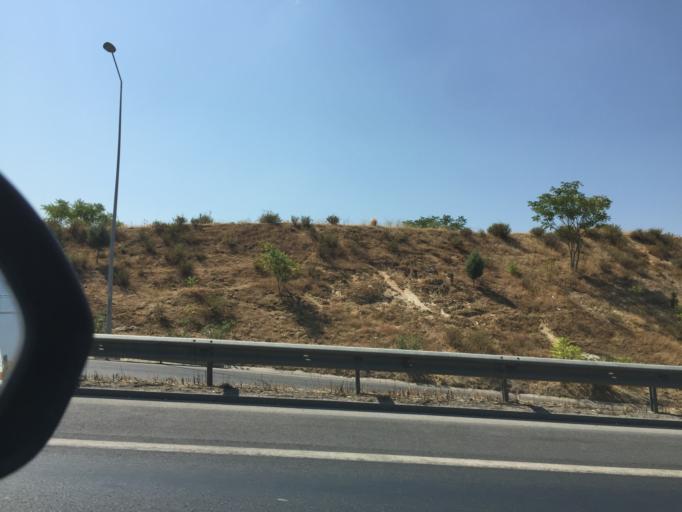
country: TR
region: Izmir
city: Karsiyaka
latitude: 38.4859
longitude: 27.1343
